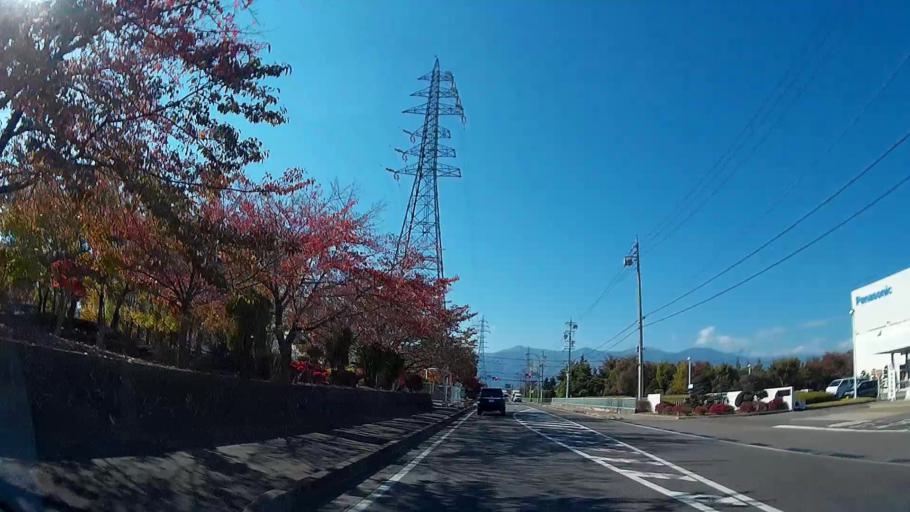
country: JP
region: Nagano
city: Matsumoto
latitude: 36.2049
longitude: 137.9361
